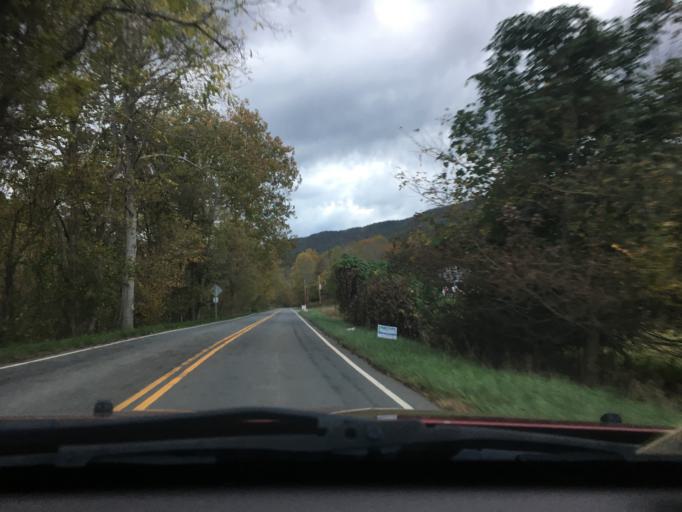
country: US
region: Virginia
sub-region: Giles County
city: Narrows
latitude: 37.2071
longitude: -80.7943
